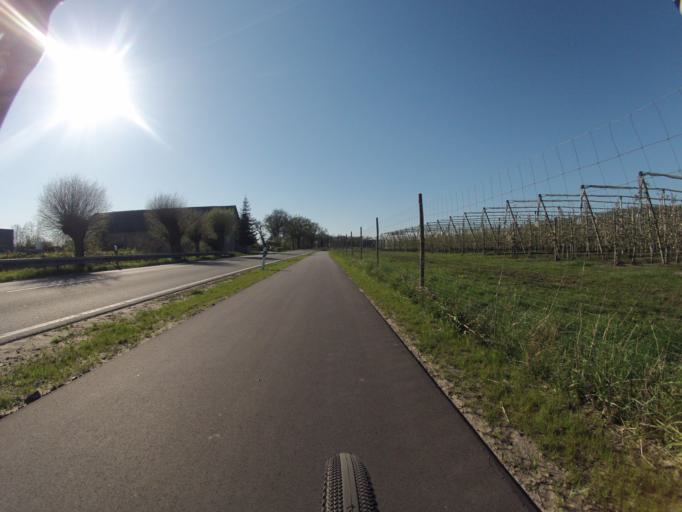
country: DE
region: North Rhine-Westphalia
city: Ibbenburen
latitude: 52.2253
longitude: 7.7217
